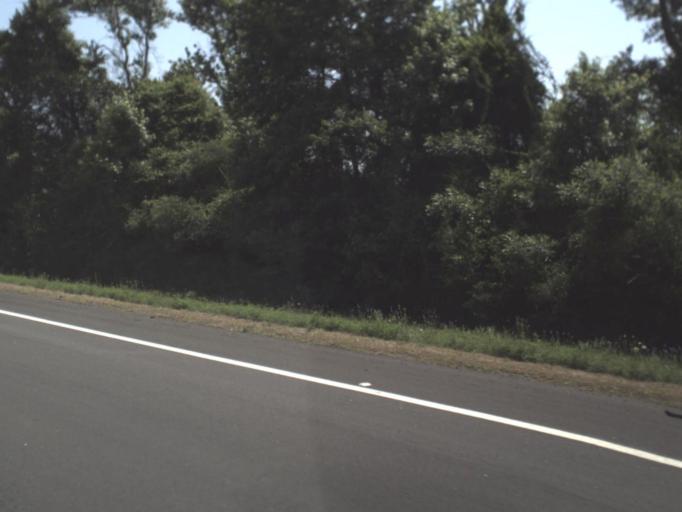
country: US
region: Georgia
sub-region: Camden County
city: Kingsland
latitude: 30.7309
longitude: -81.6611
